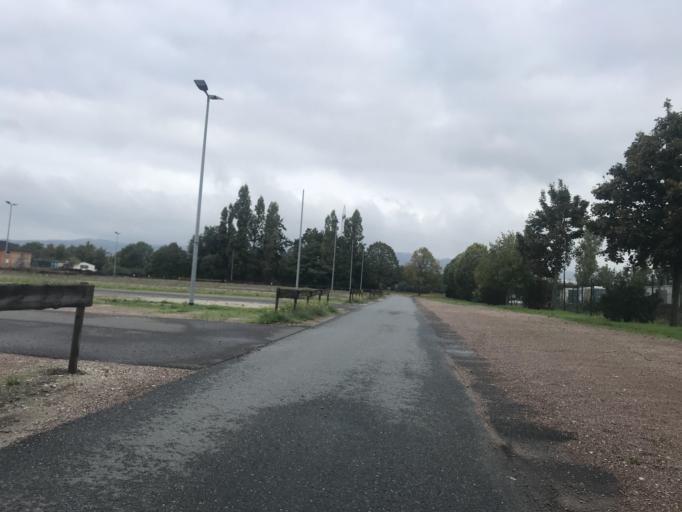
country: DE
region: Rheinland-Pfalz
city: Ingelheim am Rhein
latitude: 49.9799
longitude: 8.0406
